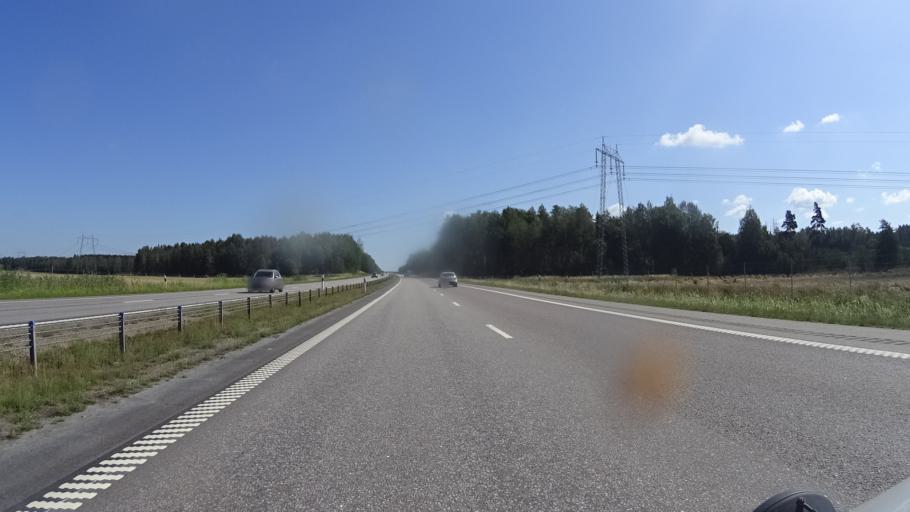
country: SE
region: OEstergoetland
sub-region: Mjolby Kommun
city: Mantorp
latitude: 58.3777
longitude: 15.3388
